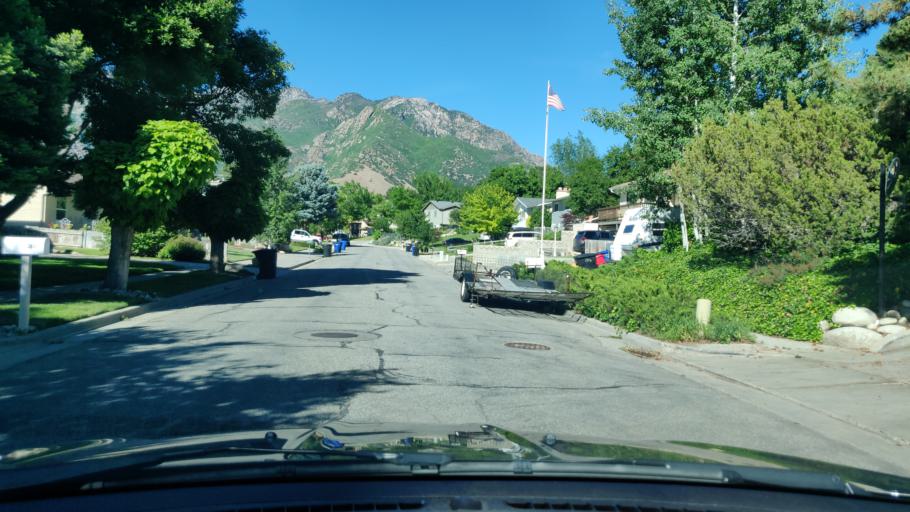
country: US
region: Utah
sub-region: Salt Lake County
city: Cottonwood Heights
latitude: 40.6144
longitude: -111.8110
